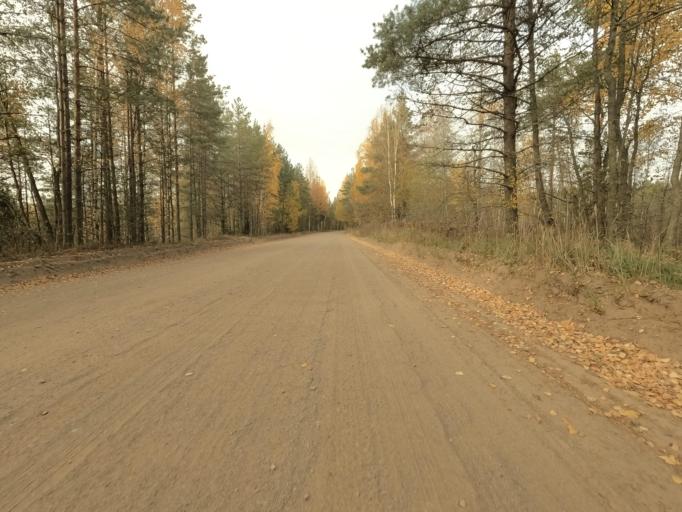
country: RU
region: Leningrad
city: Priladozhskiy
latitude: 59.6803
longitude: 31.3641
